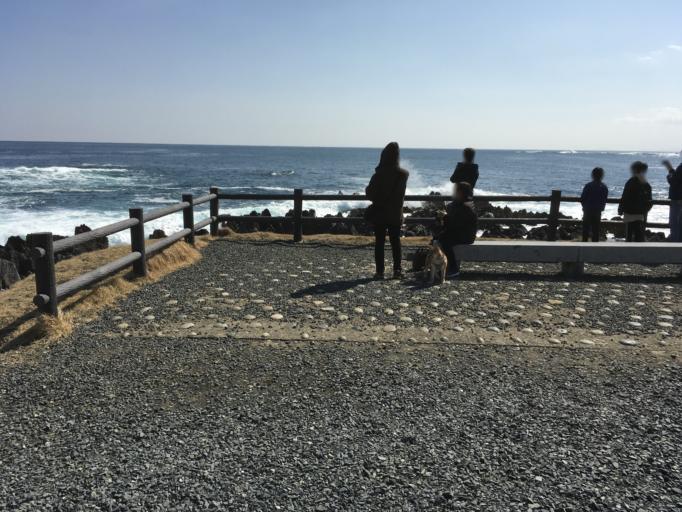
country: JP
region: Iwate
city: Ofunato
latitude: 38.8275
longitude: 141.6026
